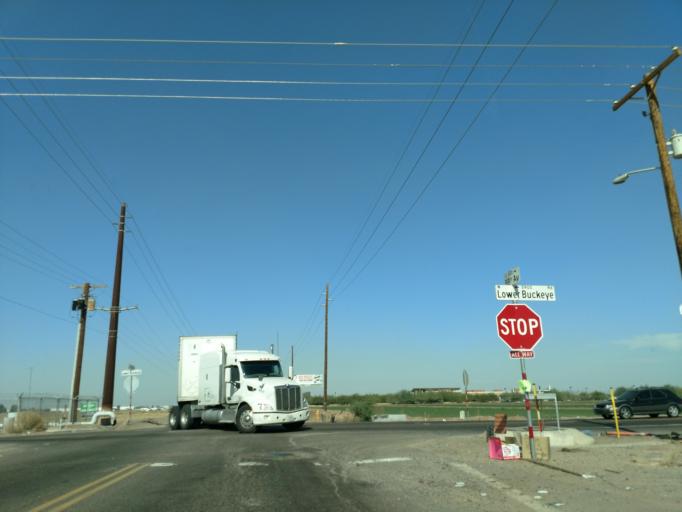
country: US
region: Arizona
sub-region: Maricopa County
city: Laveen
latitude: 33.4223
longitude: -112.1865
